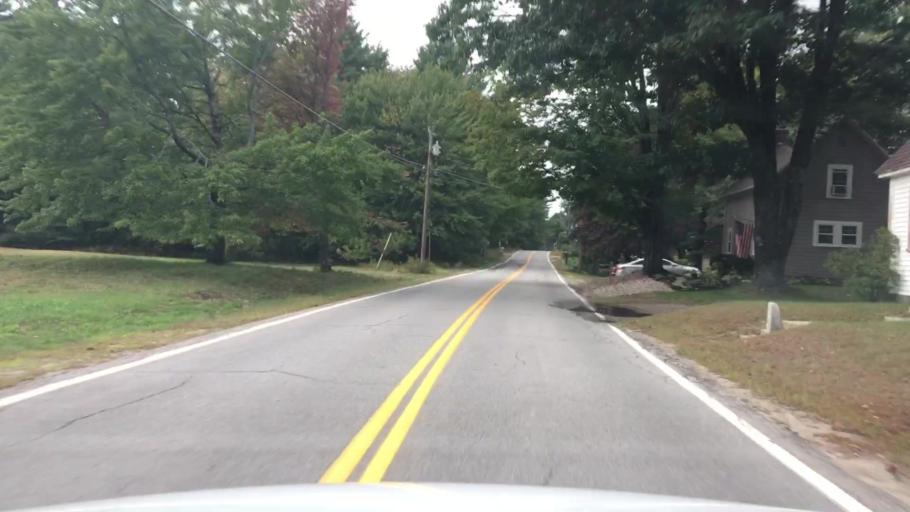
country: US
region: New Hampshire
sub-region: Carroll County
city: Effingham
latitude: 43.7123
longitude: -70.9829
